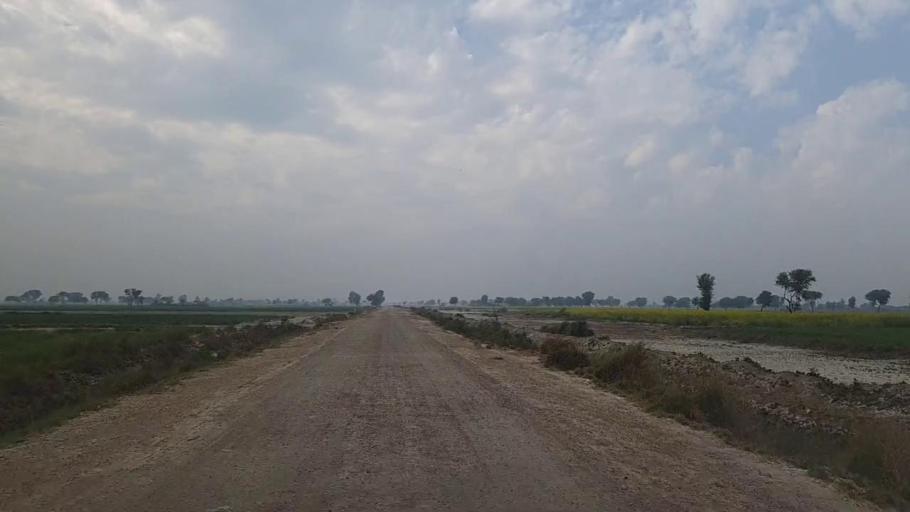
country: PK
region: Sindh
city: Nawabshah
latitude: 26.3652
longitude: 68.3994
